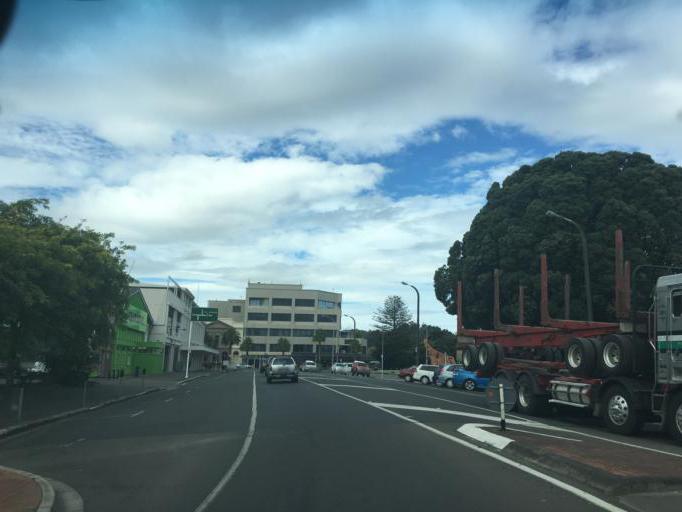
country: NZ
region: Gisborne
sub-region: Gisborne District
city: Gisborne
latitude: -38.6689
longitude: 178.0269
